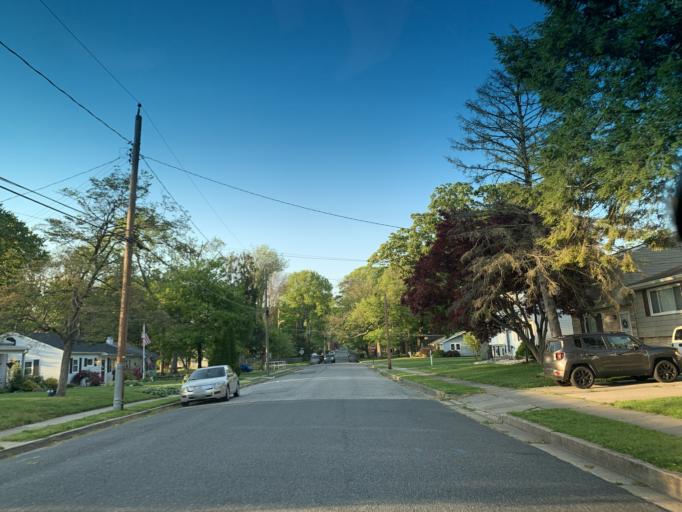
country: US
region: Maryland
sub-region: Harford County
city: Aberdeen
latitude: 39.5018
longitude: -76.1721
